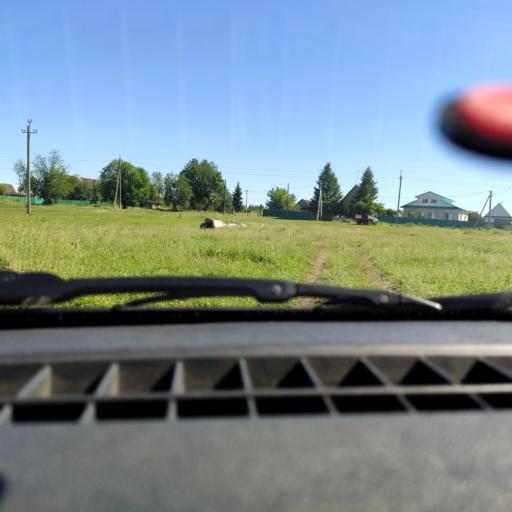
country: RU
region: Bashkortostan
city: Iglino
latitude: 54.8926
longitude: 56.4986
